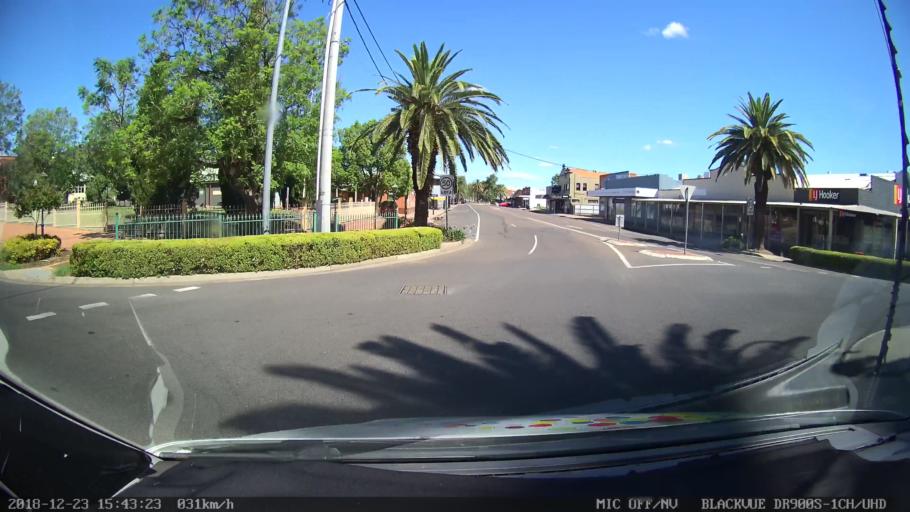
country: AU
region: New South Wales
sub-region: Tamworth Municipality
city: Tamworth
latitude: -31.0867
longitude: 150.9264
